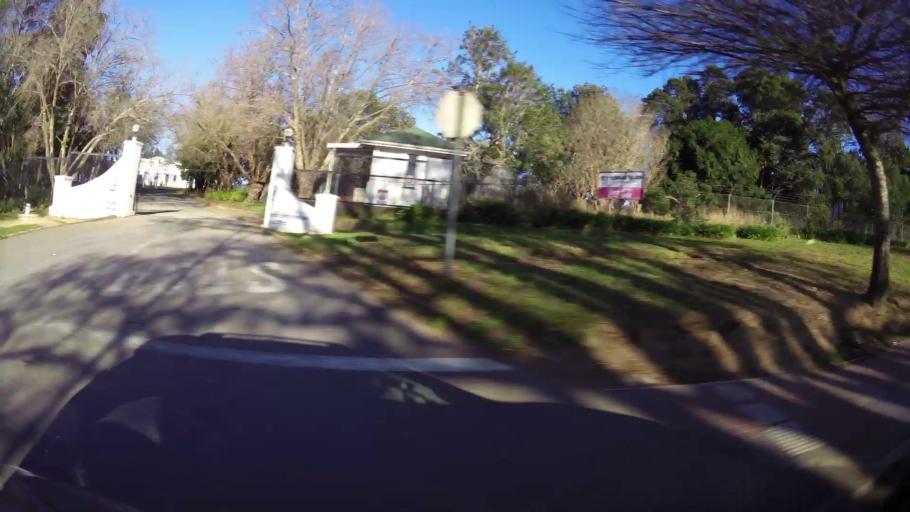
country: ZA
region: Western Cape
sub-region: Eden District Municipality
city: George
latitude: -33.9542
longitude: 22.4509
